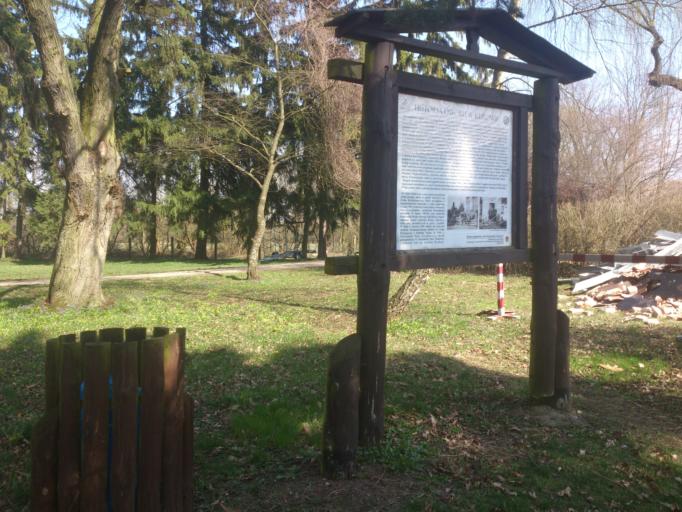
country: PL
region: Podlasie
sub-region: Powiat bialostocki
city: Tykocin
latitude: 53.1049
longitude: 22.7955
